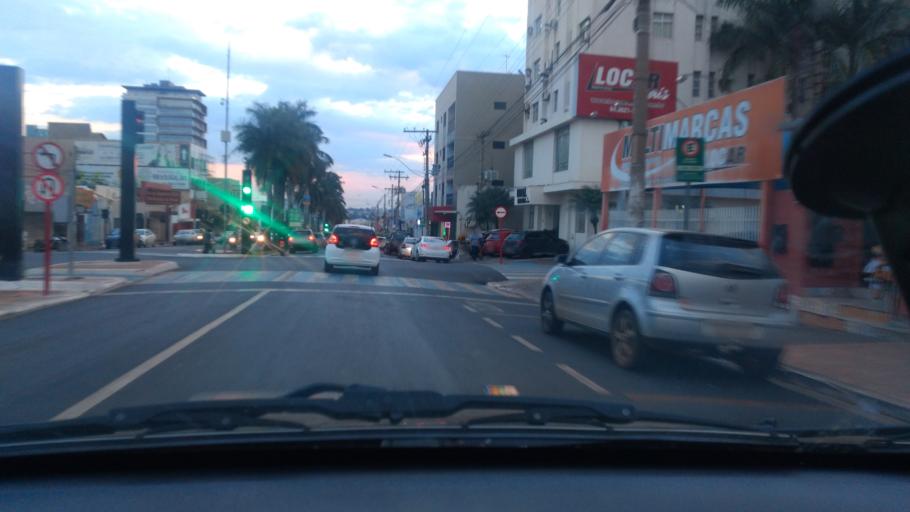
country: BR
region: Goias
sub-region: Santa Helena De Goias
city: Santa Helena de Goias
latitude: -17.7949
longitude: -50.9317
